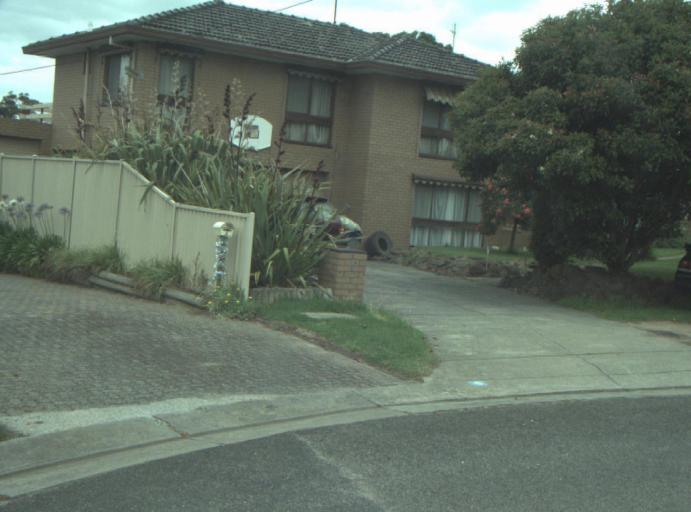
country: AU
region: Victoria
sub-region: Greater Geelong
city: Wandana Heights
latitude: -38.2068
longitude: 144.3232
